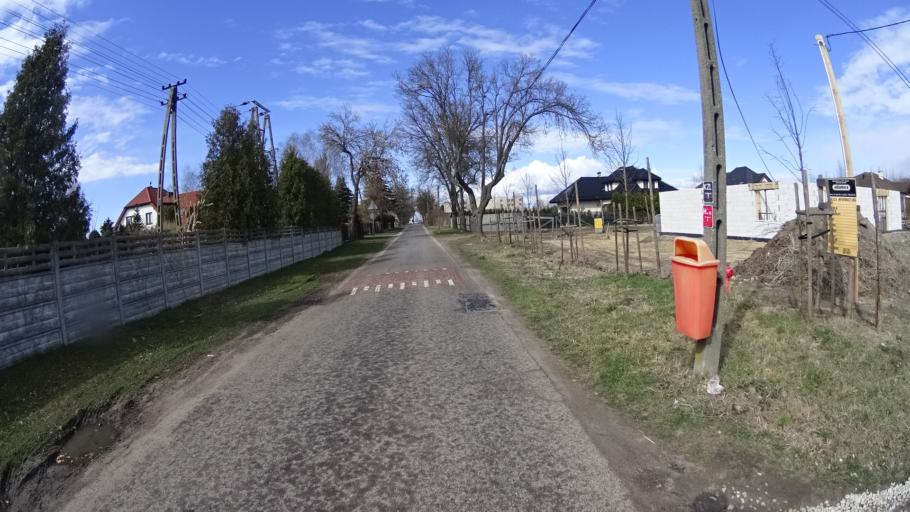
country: PL
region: Masovian Voivodeship
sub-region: Powiat warszawski zachodni
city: Jozefow
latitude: 52.2078
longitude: 20.6829
